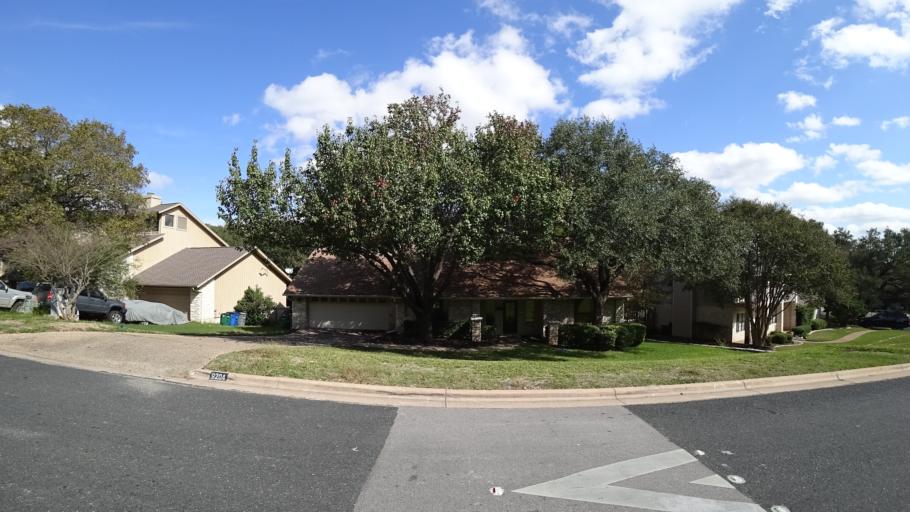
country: US
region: Texas
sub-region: Williamson County
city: Anderson Mill
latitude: 30.4219
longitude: -97.8025
